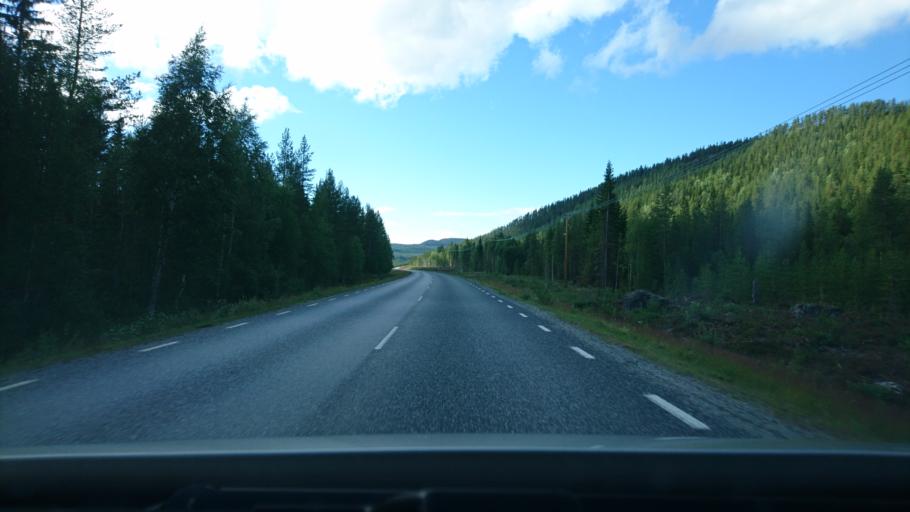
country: SE
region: Vaesterbotten
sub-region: Asele Kommun
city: Asele
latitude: 64.3106
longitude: 17.2342
